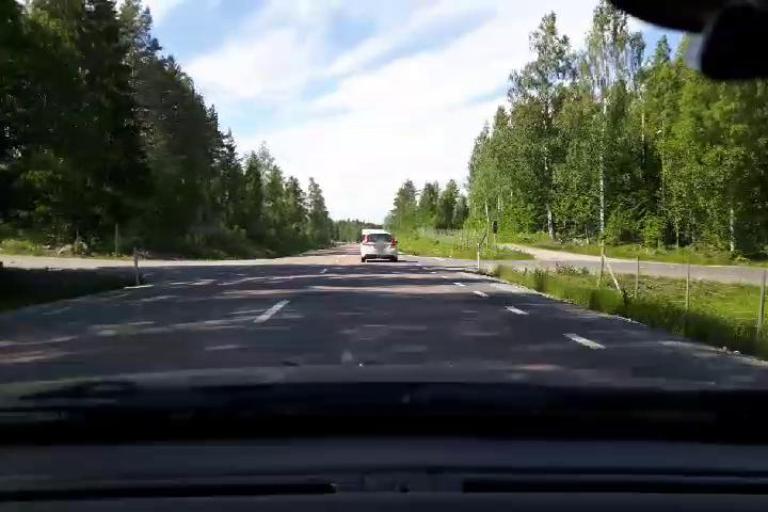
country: SE
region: Gaevleborg
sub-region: Bollnas Kommun
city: Kilafors
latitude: 61.2798
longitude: 16.5216
